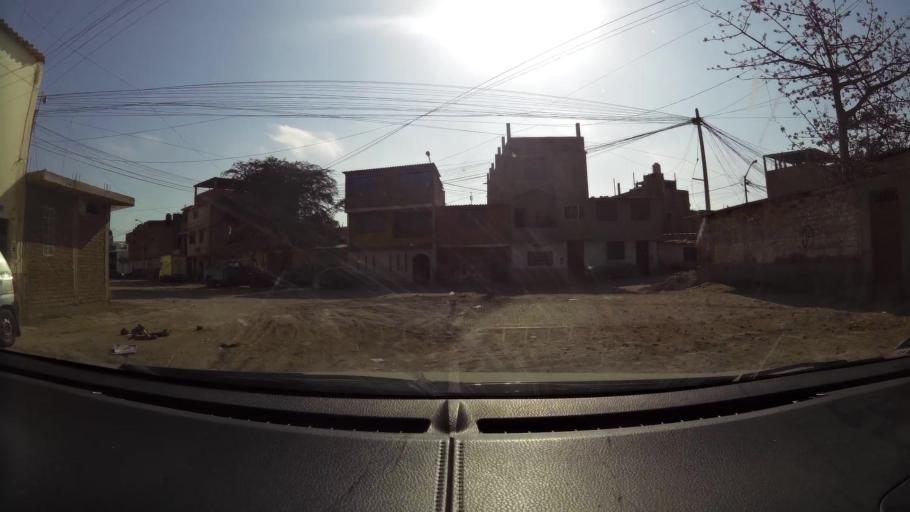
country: PE
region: Lambayeque
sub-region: Provincia de Chiclayo
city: Chiclayo
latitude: -6.7667
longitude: -79.8473
